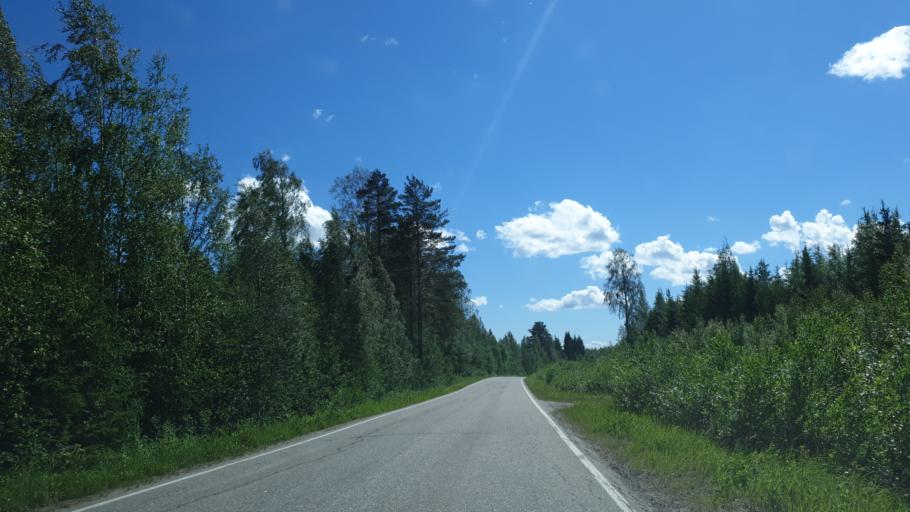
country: FI
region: Northern Savo
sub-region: Koillis-Savo
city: Kaavi
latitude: 62.9905
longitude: 28.5046
